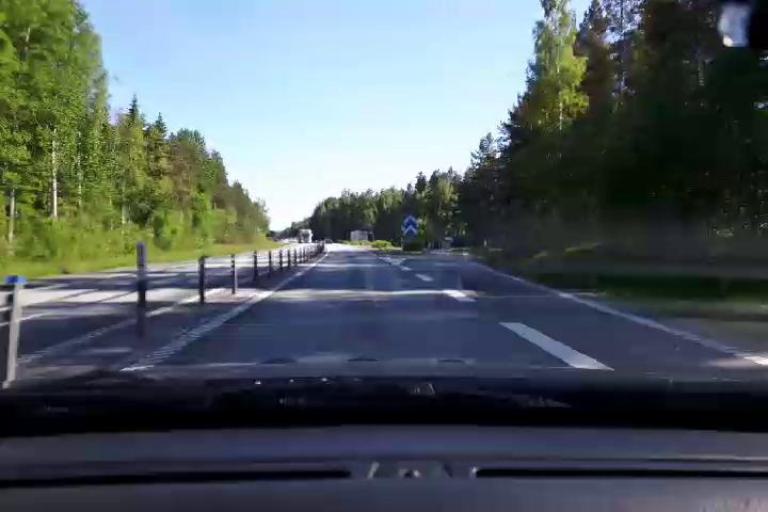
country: SE
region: Gaevleborg
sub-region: Gavle Kommun
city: Norrsundet
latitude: 61.0082
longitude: 16.9839
